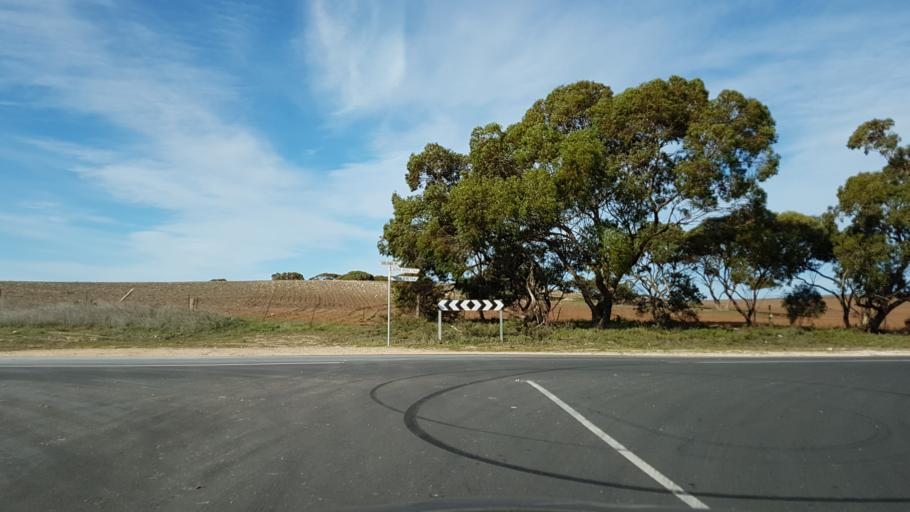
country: AU
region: South Australia
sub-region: Murray Bridge
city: Tailem Bend
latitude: -35.1830
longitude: 139.4652
